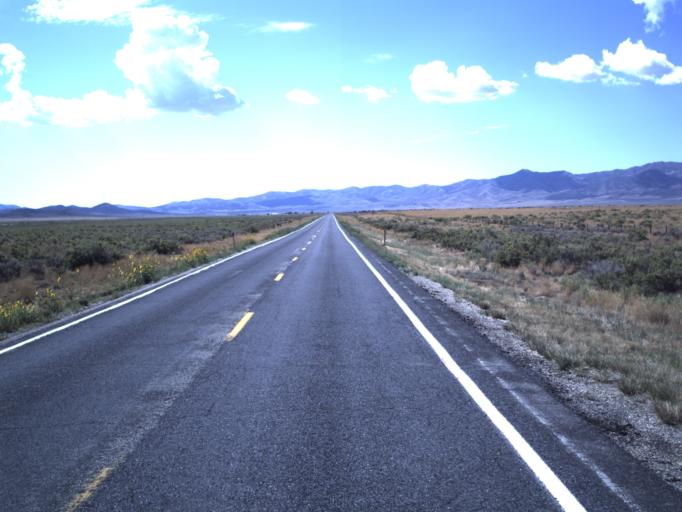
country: US
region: Utah
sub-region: Tooele County
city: Tooele
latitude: 40.1361
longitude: -112.4308
